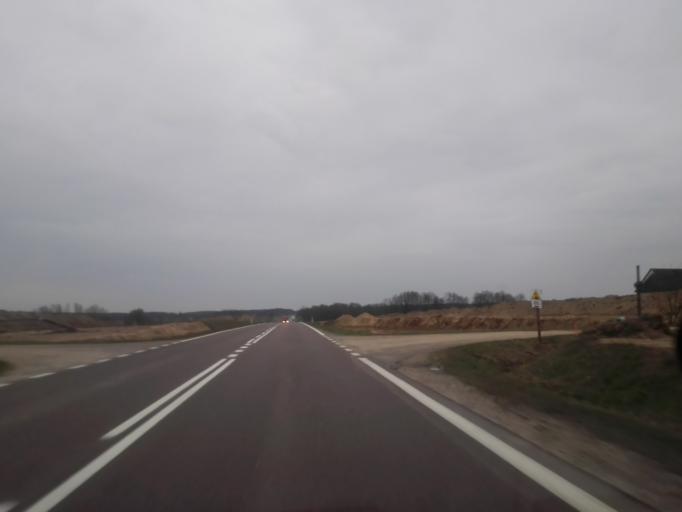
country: PL
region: Podlasie
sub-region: Powiat grajewski
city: Szczuczyn
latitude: 53.5392
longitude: 22.2643
